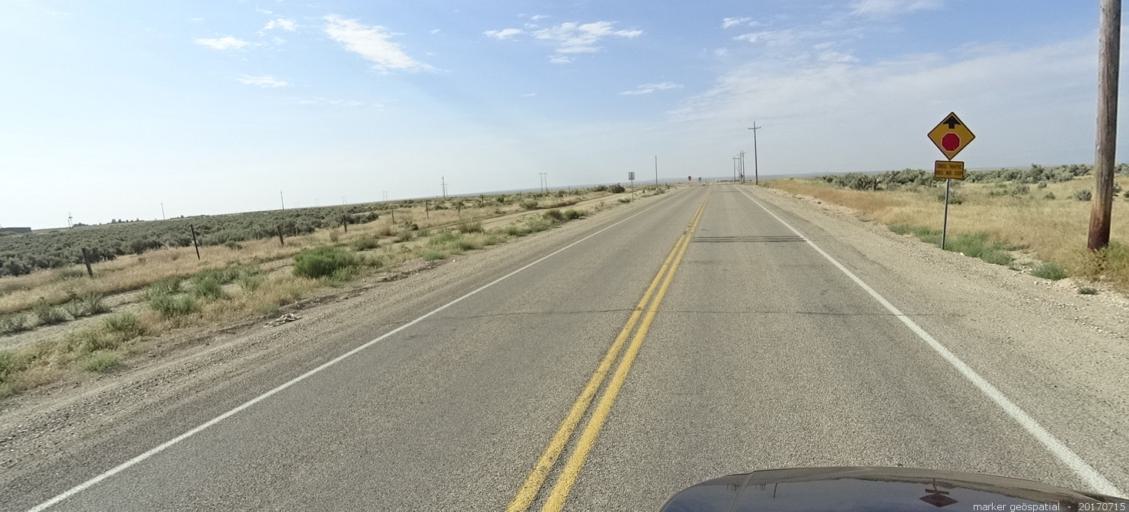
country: US
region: Idaho
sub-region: Ada County
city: Boise
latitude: 43.4609
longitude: -116.2344
